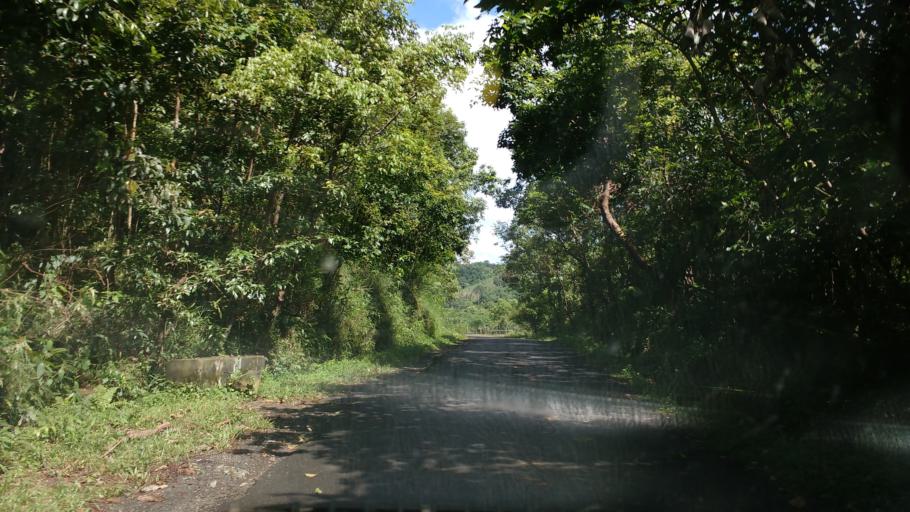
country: IN
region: Meghalaya
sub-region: East Khasi Hills
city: Cherrapunji
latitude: 25.2181
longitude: 91.9223
